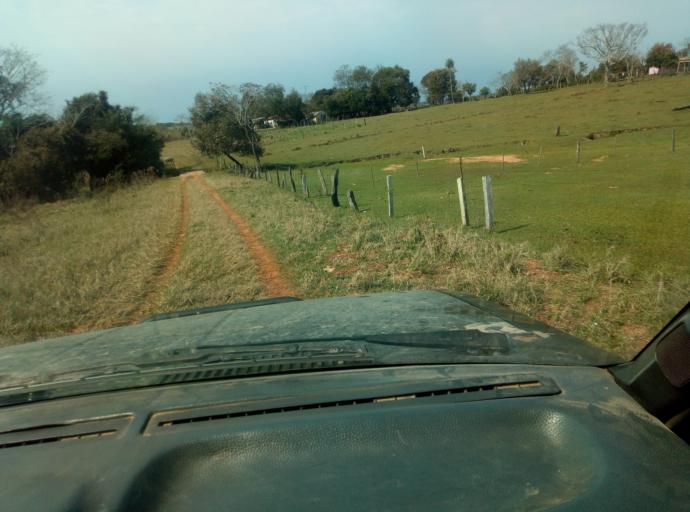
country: PY
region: Caaguazu
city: Doctor Cecilio Baez
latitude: -25.1444
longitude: -56.2413
